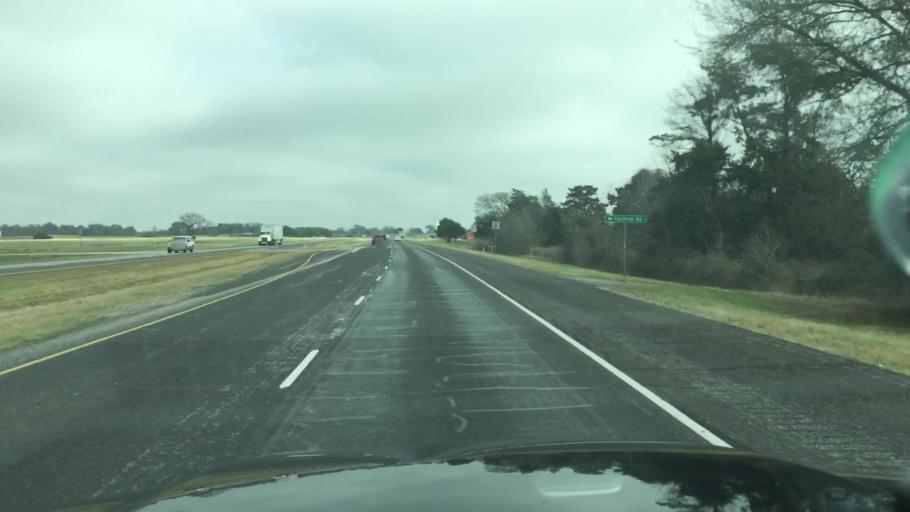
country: US
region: Texas
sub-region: Burleson County
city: Somerville
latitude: 30.1508
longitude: -96.6732
